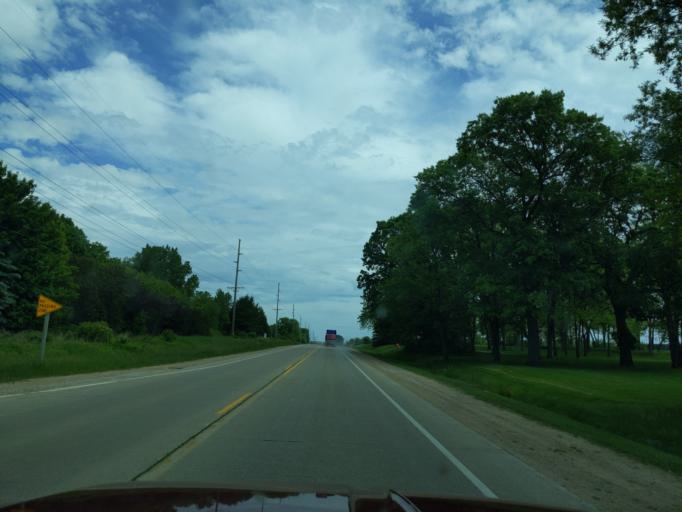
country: US
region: Wisconsin
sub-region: Dane County
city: Windsor
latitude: 43.1914
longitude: -89.2821
